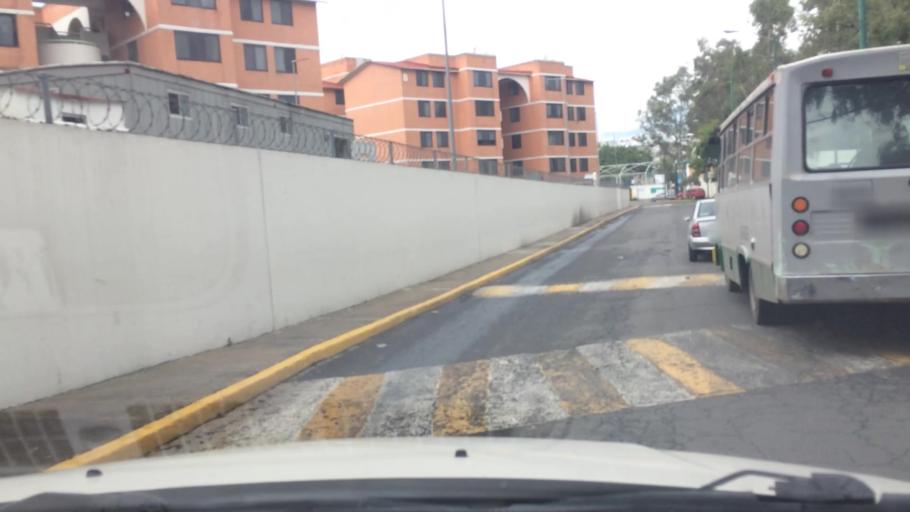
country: MX
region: Mexico City
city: Xochimilco
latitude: 19.2966
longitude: -99.1013
